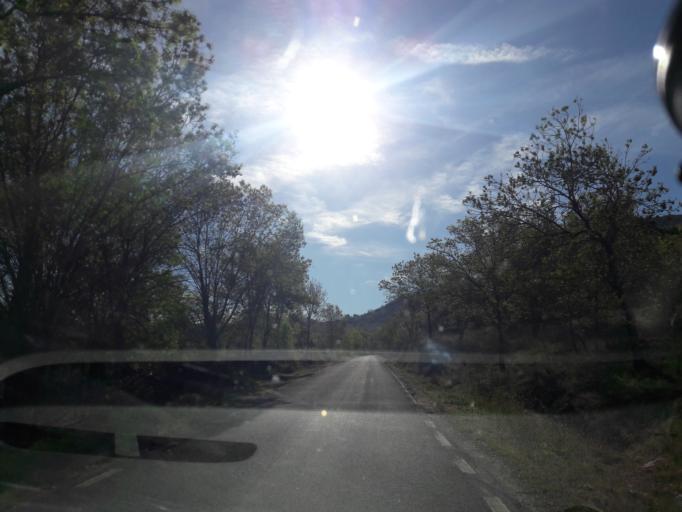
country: ES
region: Castille and Leon
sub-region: Provincia de Salamanca
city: Sanchotello
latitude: 40.4361
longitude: -5.7627
